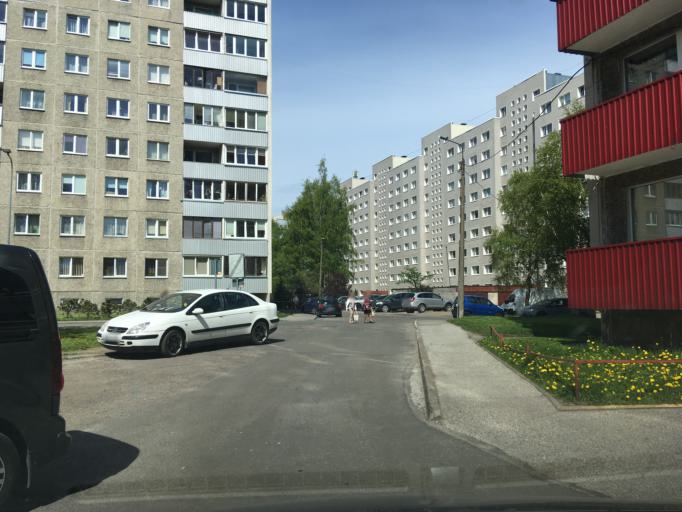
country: EE
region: Harju
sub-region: Tallinna linn
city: Kose
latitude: 59.4346
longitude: 24.8236
